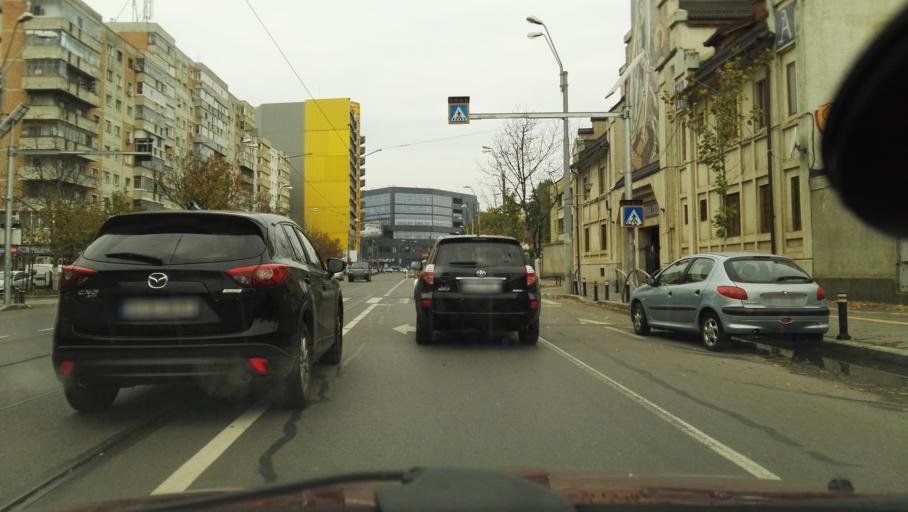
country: RO
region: Bucuresti
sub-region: Municipiul Bucuresti
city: Bucuresti
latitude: 44.4007
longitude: 26.1022
